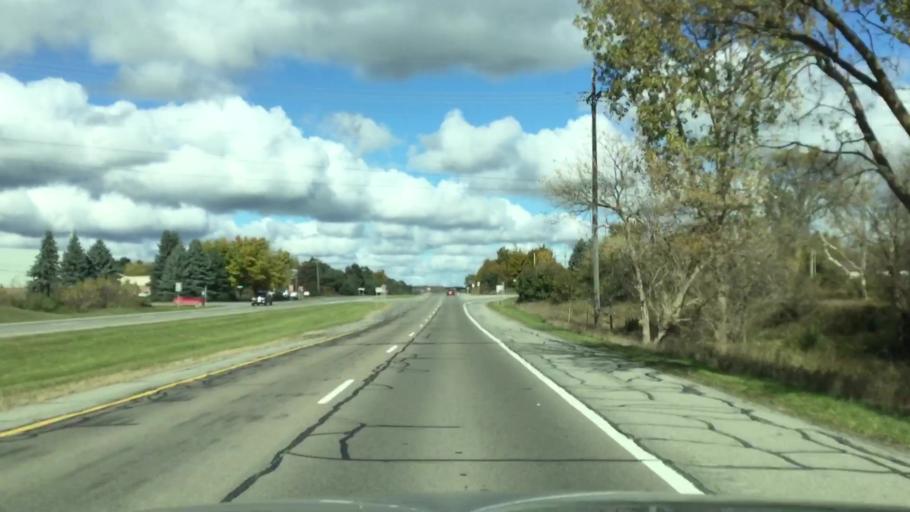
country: US
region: Michigan
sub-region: Oakland County
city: Oxford
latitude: 42.8596
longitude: -83.2883
